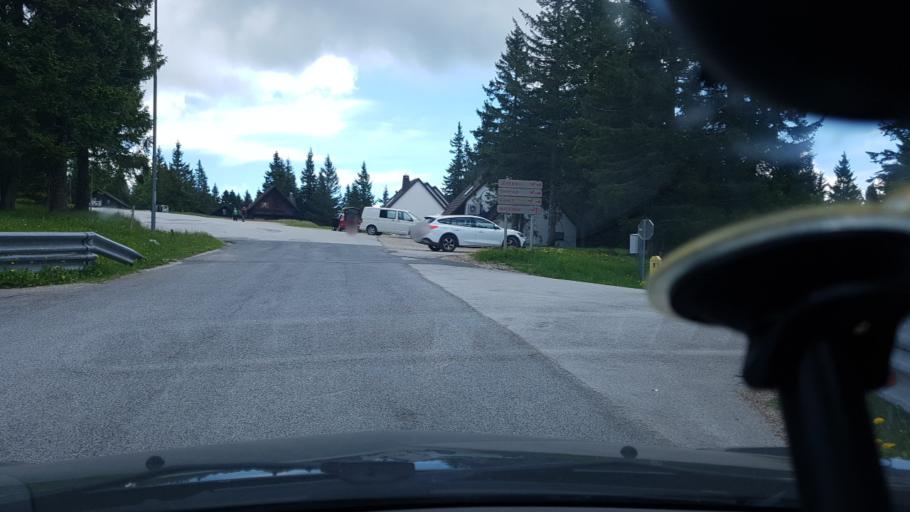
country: SI
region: Mislinja
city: Mislinja
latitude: 46.4516
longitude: 15.3282
